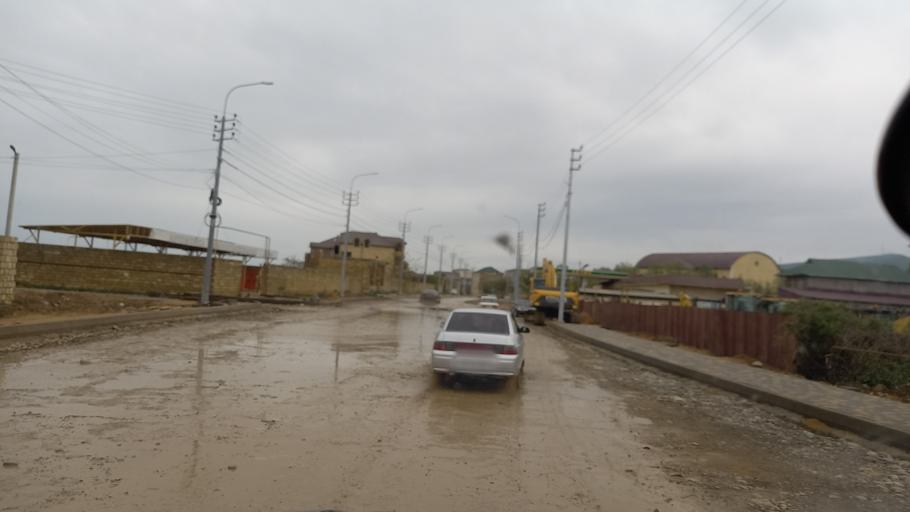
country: RU
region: Dagestan
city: Derbent
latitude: 42.0960
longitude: 48.2878
